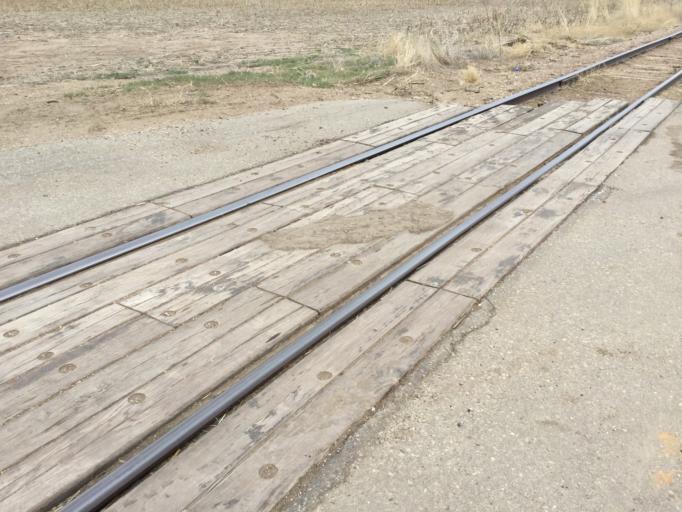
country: US
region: Kansas
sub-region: Ottawa County
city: Minneapolis
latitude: 39.1511
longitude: -97.7246
